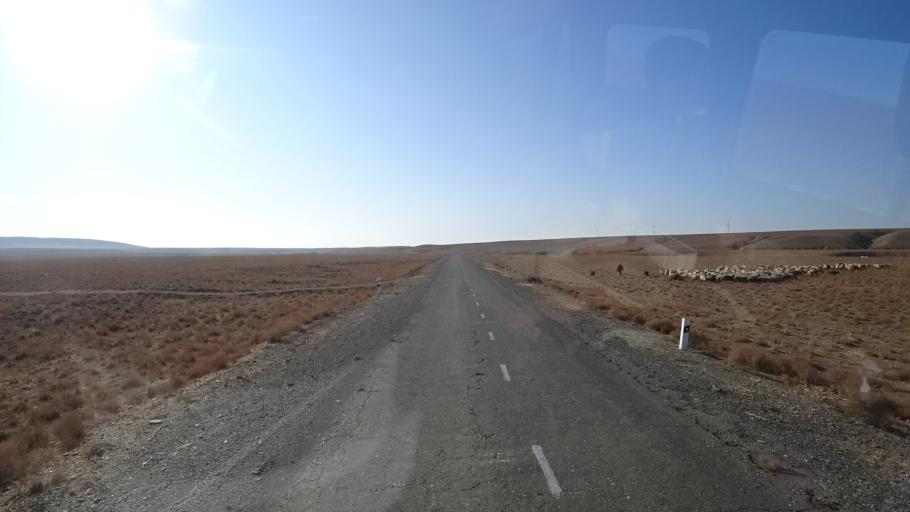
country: UZ
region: Navoiy
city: Beshrabot
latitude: 40.2603
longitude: 65.4873
